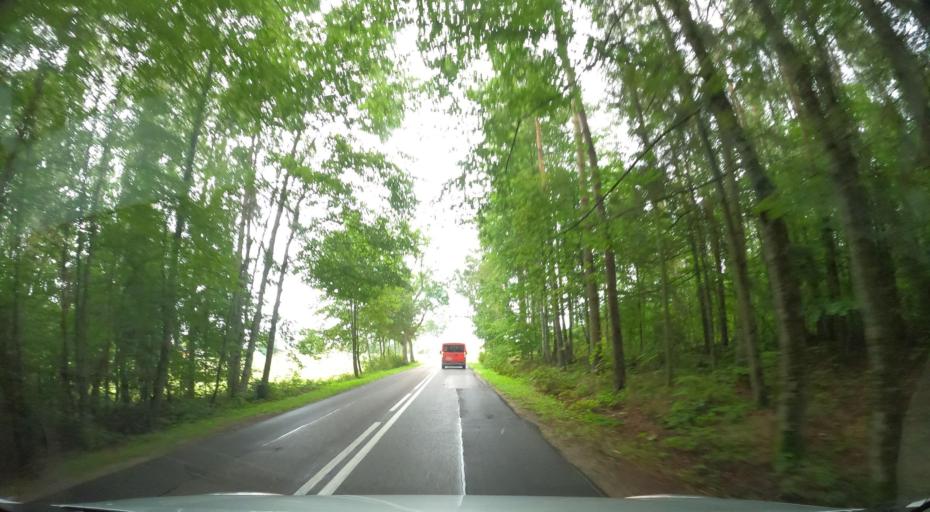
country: PL
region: Pomeranian Voivodeship
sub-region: Powiat wejherowski
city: Luzino
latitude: 54.4932
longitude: 18.1342
